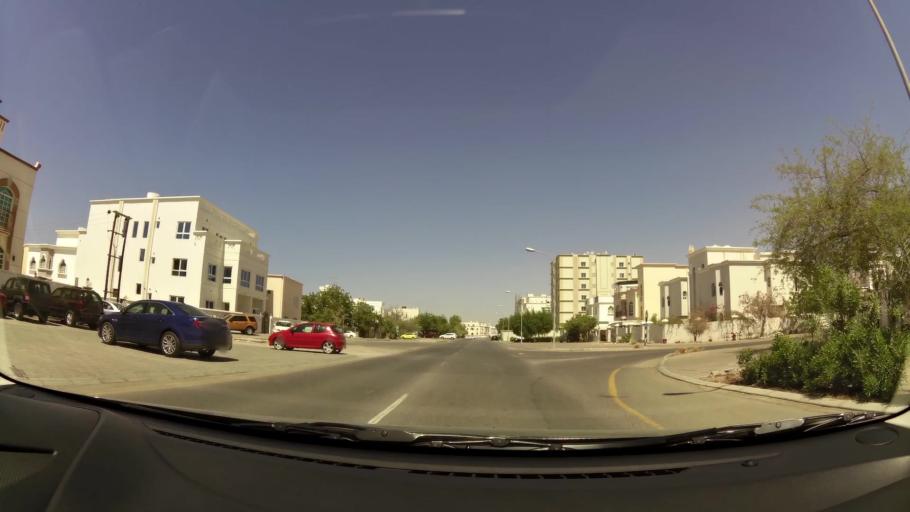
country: OM
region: Muhafazat Masqat
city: Bawshar
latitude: 23.5969
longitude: 58.3579
